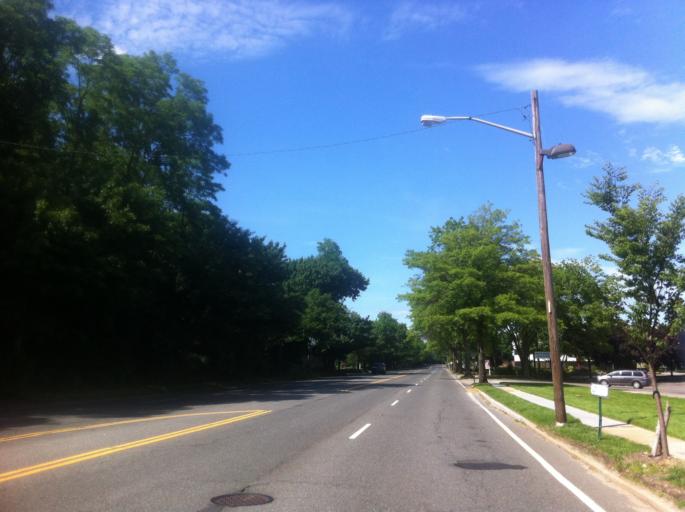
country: US
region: New York
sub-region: Nassau County
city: Syosset
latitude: 40.8117
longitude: -73.5142
